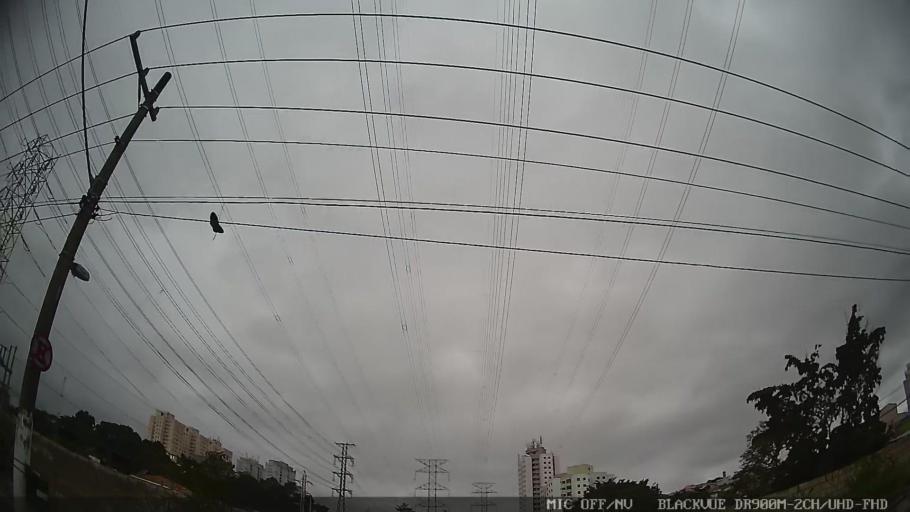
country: BR
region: Sao Paulo
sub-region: Osasco
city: Osasco
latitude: -23.4946
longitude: -46.7463
